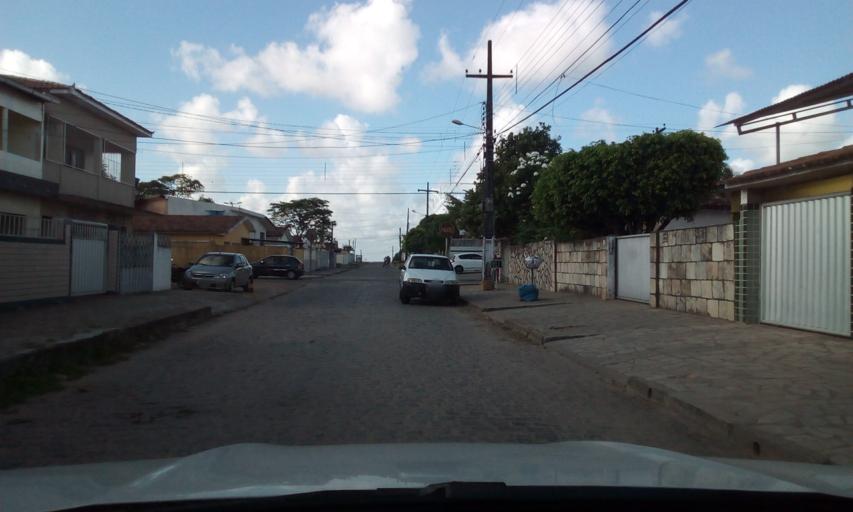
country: BR
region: Paraiba
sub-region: Bayeux
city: Bayeux
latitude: -7.1595
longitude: -34.8985
